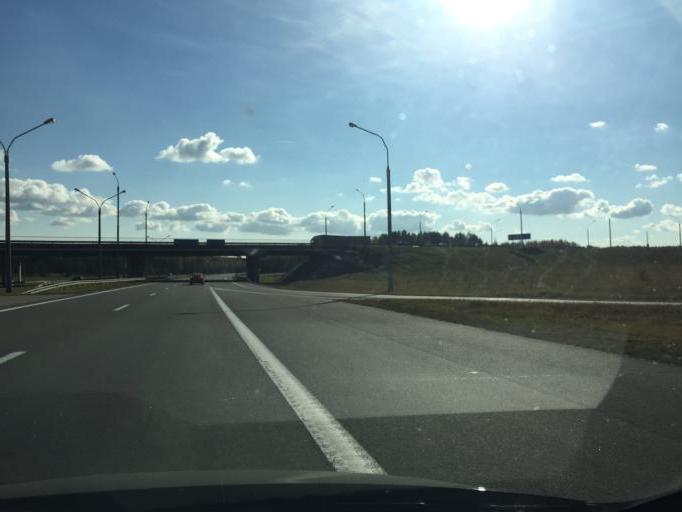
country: BY
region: Minsk
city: Slabada
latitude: 53.9503
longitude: 27.9762
